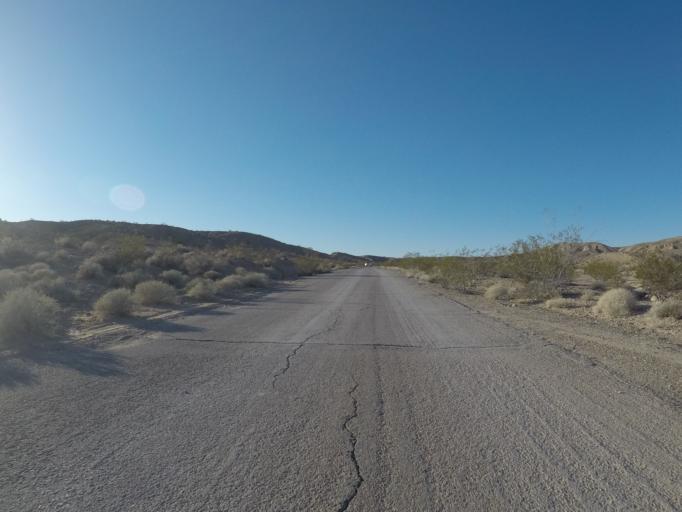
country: US
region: Nevada
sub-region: Clark County
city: Moapa Valley
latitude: 36.3880
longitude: -114.4166
